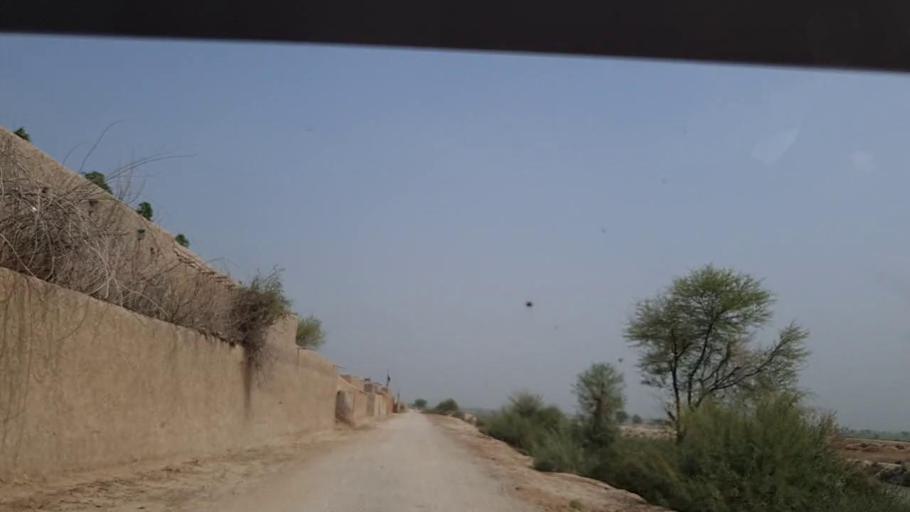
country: PK
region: Sindh
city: Khairpur Nathan Shah
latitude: 27.0252
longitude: 67.6727
